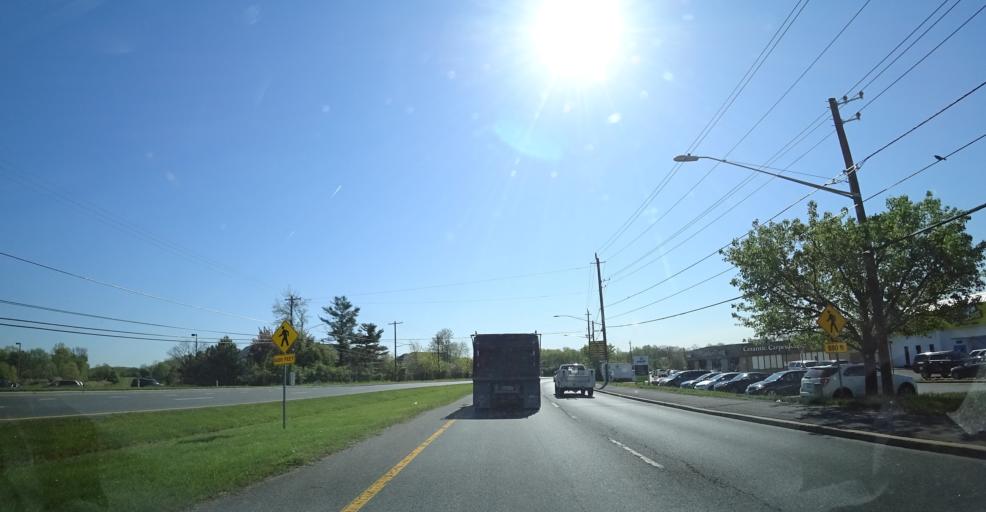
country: US
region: Maryland
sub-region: Montgomery County
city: Derwood
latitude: 39.1063
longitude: -77.1472
